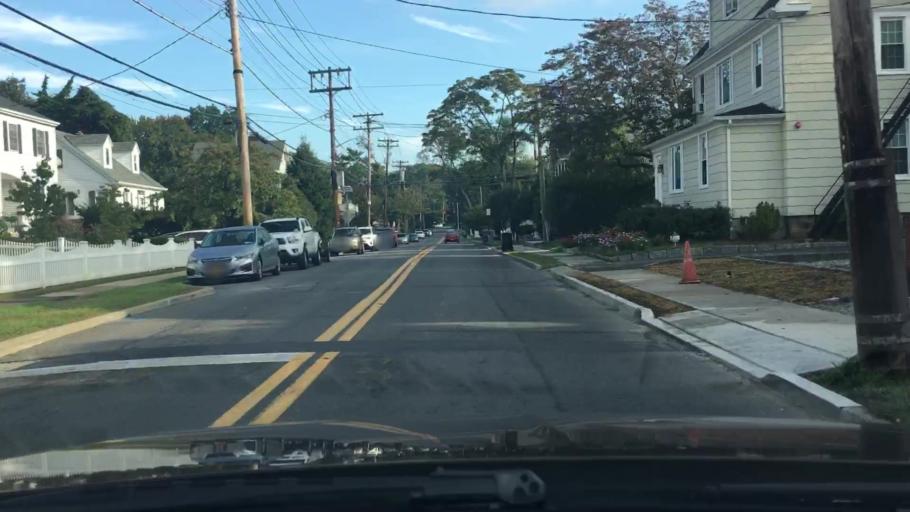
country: US
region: New York
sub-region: Westchester County
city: Rye
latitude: 40.9783
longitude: -73.6791
